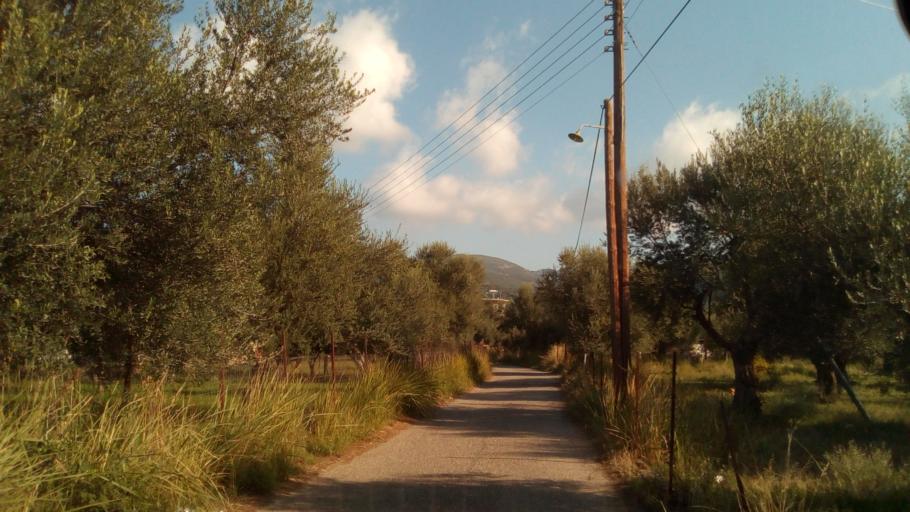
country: GR
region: West Greece
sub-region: Nomos Aitolias kai Akarnanias
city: Nafpaktos
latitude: 38.4143
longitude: 21.8889
